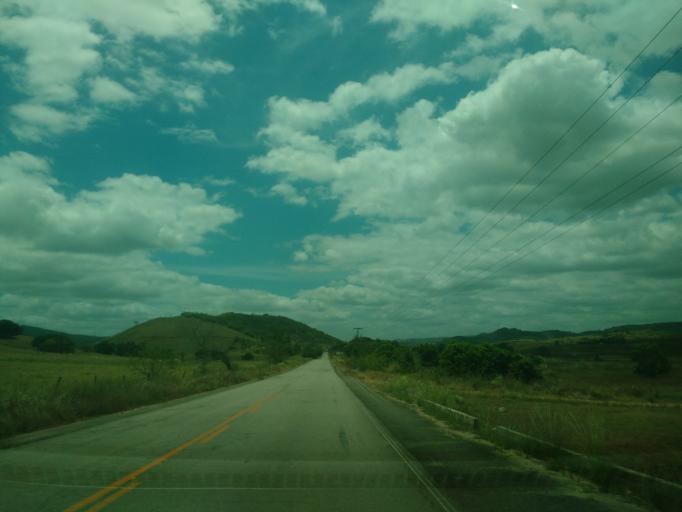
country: BR
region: Alagoas
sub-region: Uniao Dos Palmares
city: Uniao dos Palmares
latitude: -9.1426
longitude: -36.0758
